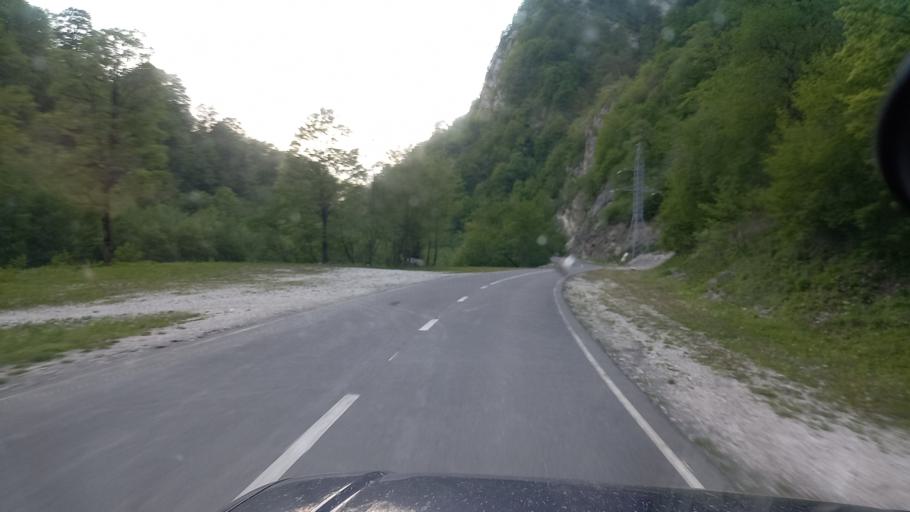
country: RU
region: Ingushetiya
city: Galashki
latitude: 42.9124
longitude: 44.9934
